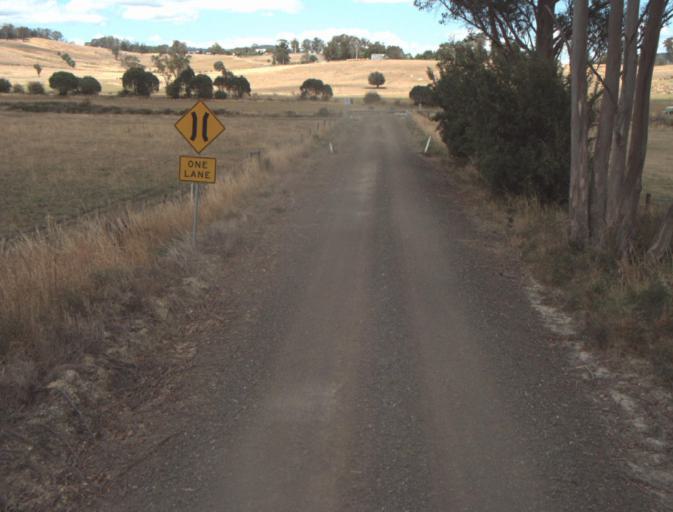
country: AU
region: Tasmania
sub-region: Launceston
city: Mayfield
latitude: -41.2113
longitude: 147.1495
